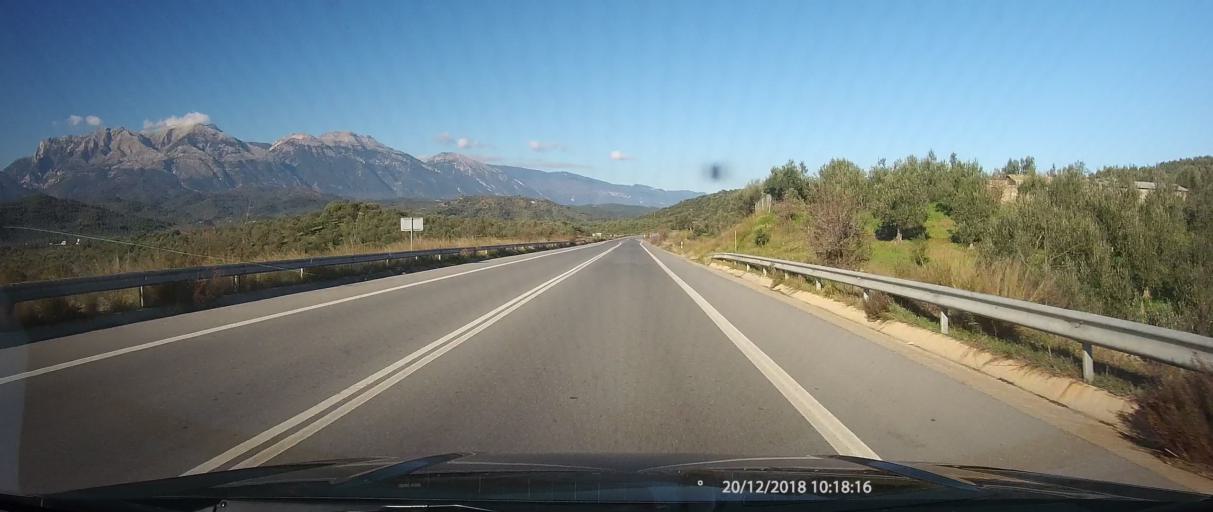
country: GR
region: Peloponnese
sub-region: Nomos Lakonias
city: Magoula
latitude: 37.1151
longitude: 22.4271
